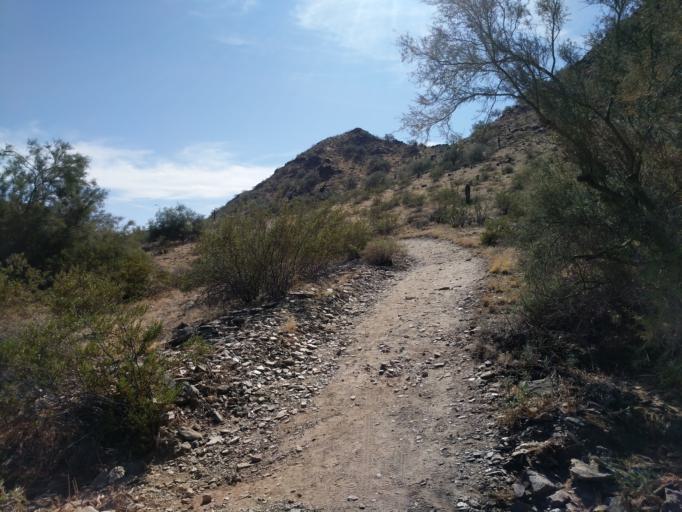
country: US
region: Arizona
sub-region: Maricopa County
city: Glendale
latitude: 33.5949
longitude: -112.0665
